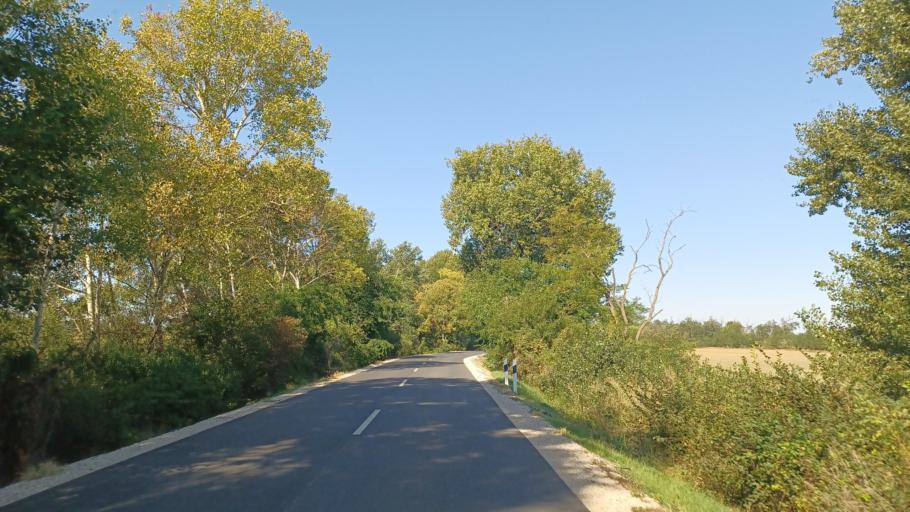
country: HU
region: Fejer
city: Alap
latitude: 46.7473
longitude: 18.6871
